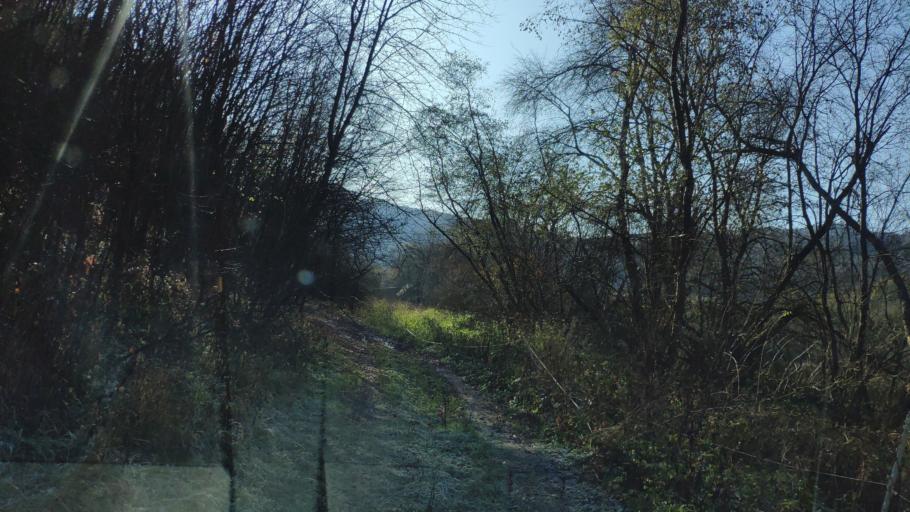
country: SK
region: Presovsky
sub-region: Okres Presov
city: Presov
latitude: 48.9006
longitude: 21.2057
